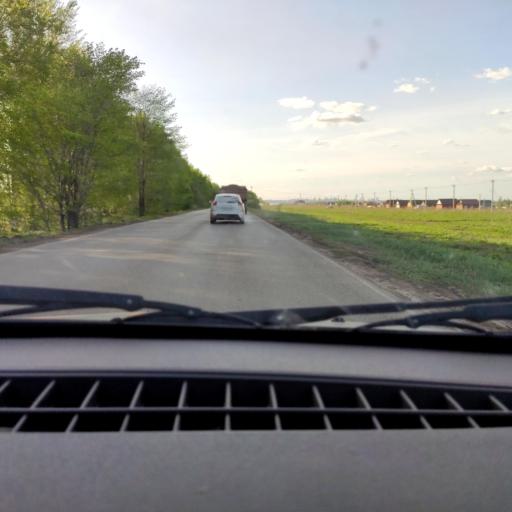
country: RU
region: Bashkortostan
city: Kabakovo
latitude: 54.6732
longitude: 56.1446
